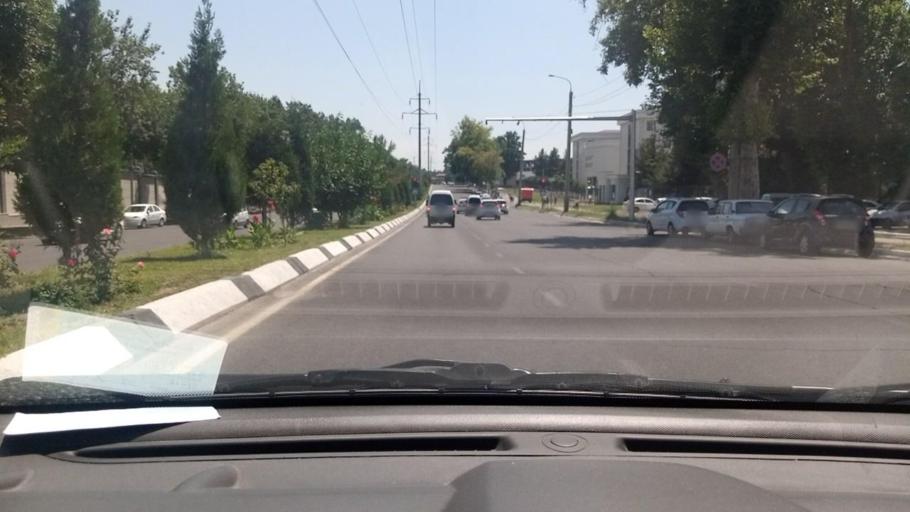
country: UZ
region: Toshkent Shahri
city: Tashkent
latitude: 41.2878
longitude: 69.1943
